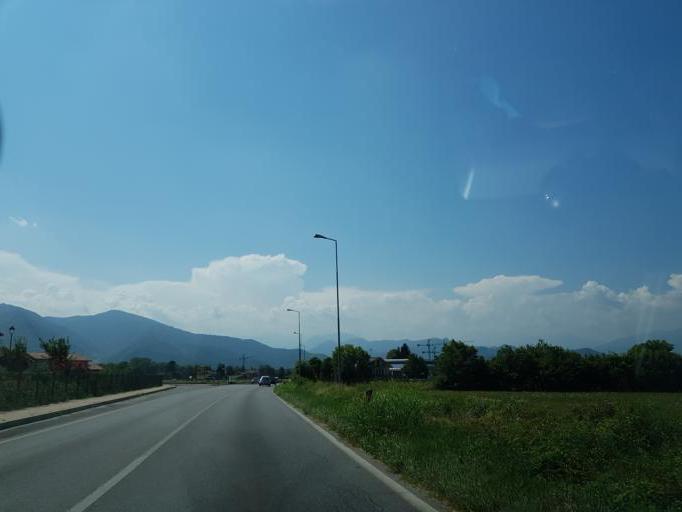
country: IT
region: Piedmont
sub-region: Provincia di Cuneo
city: San Rocco
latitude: 44.3982
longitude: 7.4709
